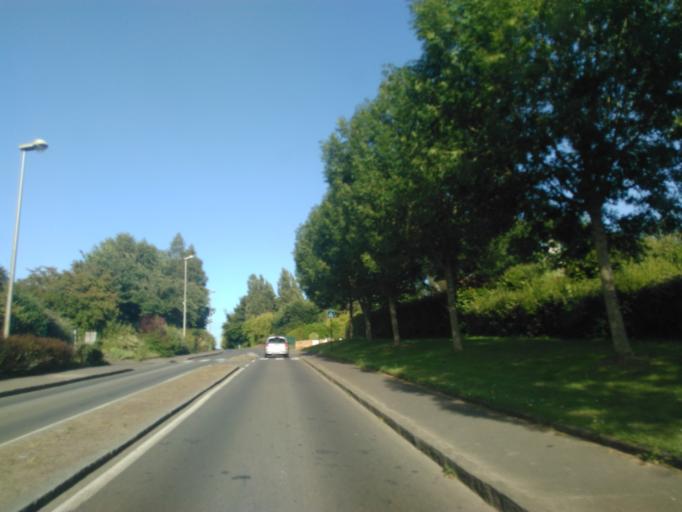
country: FR
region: Brittany
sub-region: Departement d'Ille-et-Vilaine
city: Geveze
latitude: 48.2213
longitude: -1.7995
